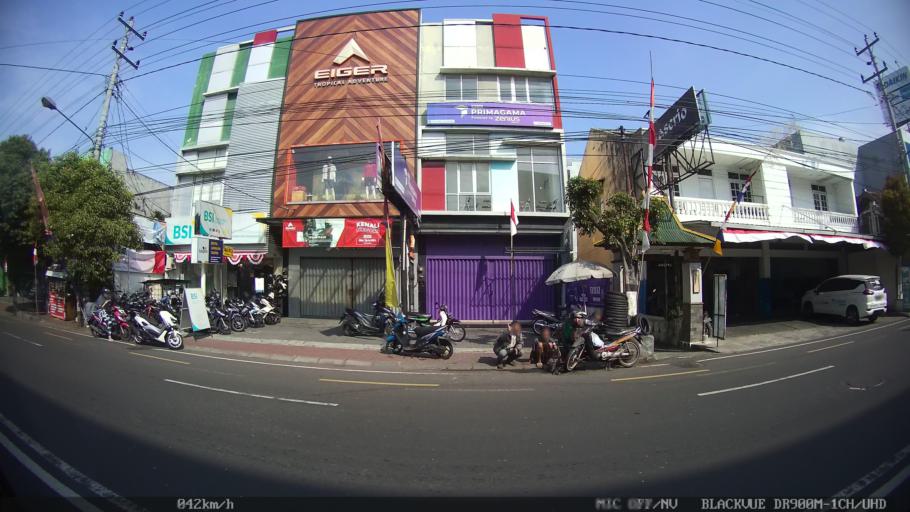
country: ID
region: Daerah Istimewa Yogyakarta
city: Yogyakarta
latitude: -7.7985
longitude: 110.3521
